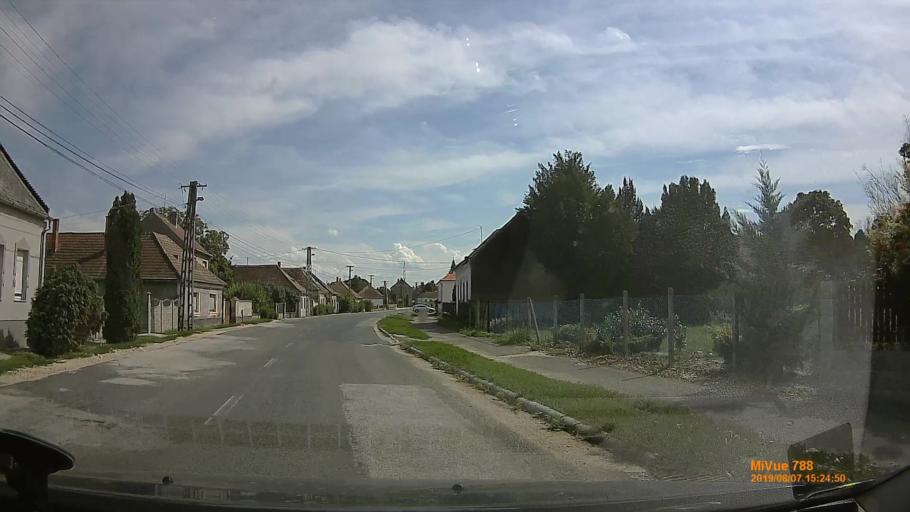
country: HU
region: Vas
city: Buk
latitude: 47.3083
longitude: 16.8328
